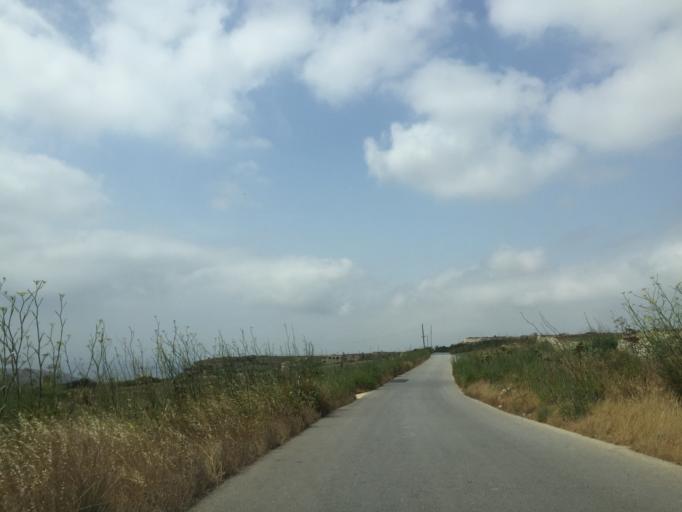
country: MT
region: L-Imgarr
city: Imgarr
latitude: 35.8954
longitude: 14.3616
